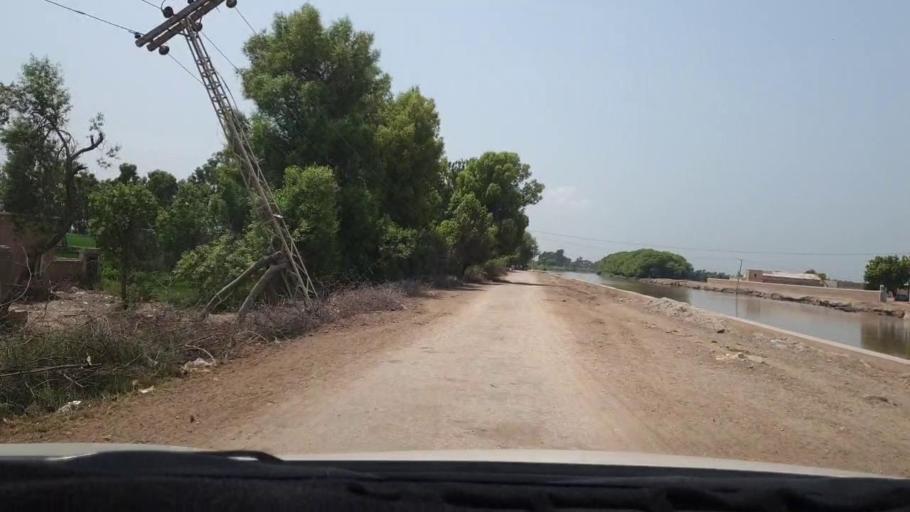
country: PK
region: Sindh
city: Dokri
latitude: 27.3233
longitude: 68.1083
